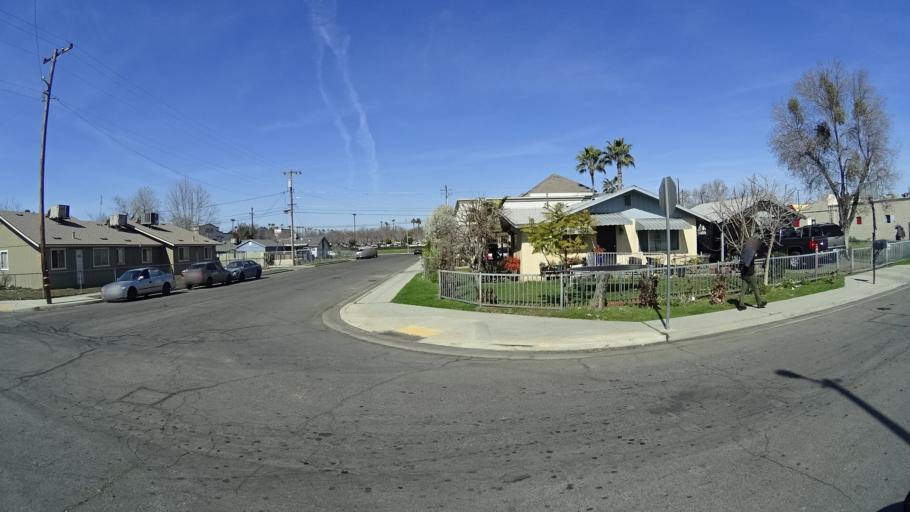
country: US
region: California
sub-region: Fresno County
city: Clovis
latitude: 36.8435
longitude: -119.7919
